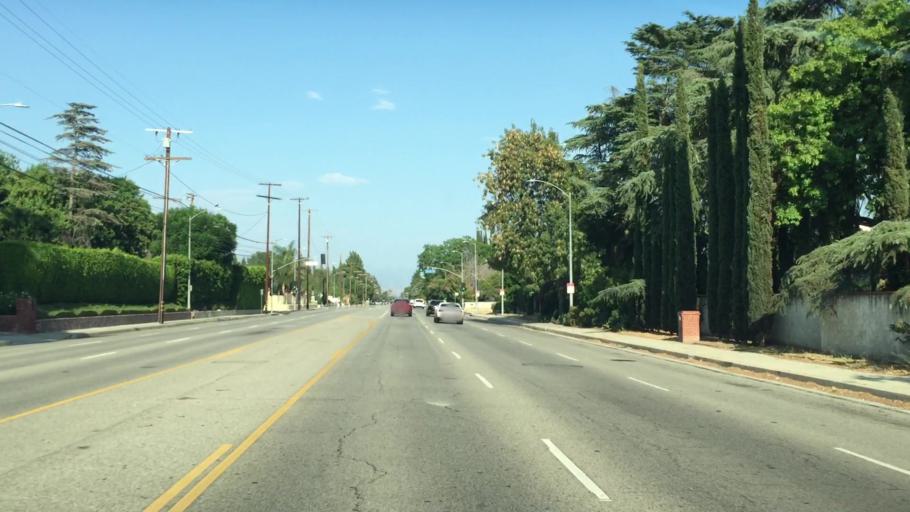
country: US
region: California
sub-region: Los Angeles County
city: Northridge
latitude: 34.2358
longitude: -118.5170
